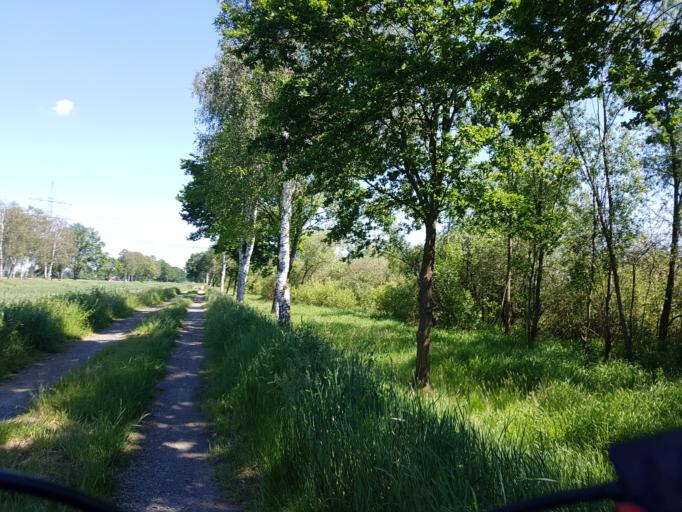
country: DE
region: Brandenburg
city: Merzdorf
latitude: 51.4302
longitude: 13.5479
